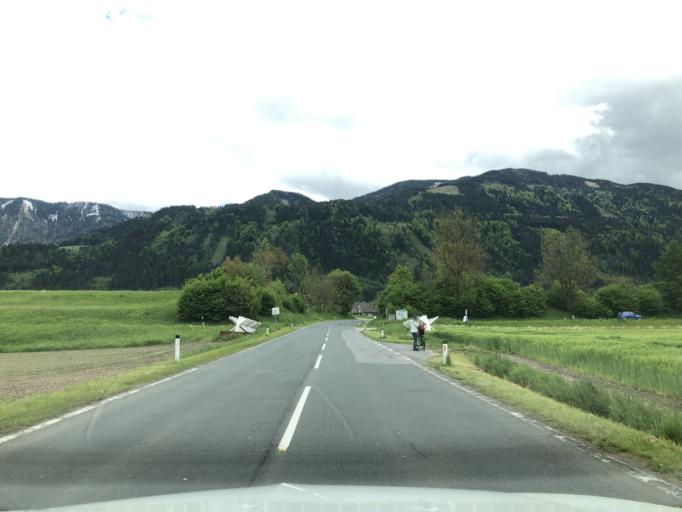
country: AT
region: Carinthia
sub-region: Politischer Bezirk Villach Land
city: Arnoldstein
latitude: 46.5525
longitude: 13.7880
